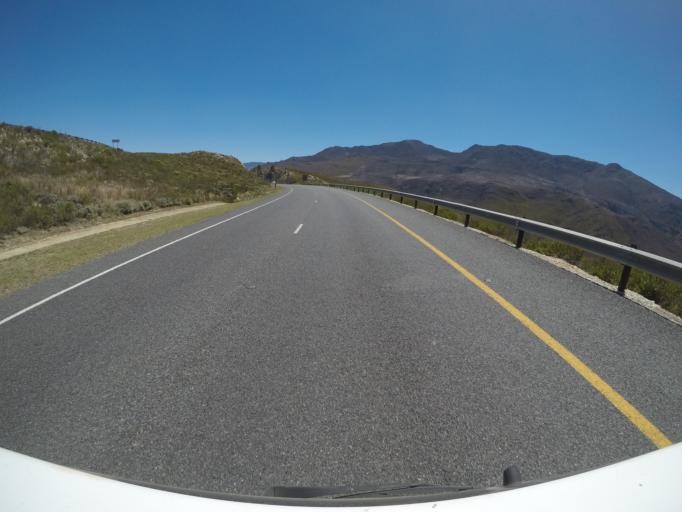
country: ZA
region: Western Cape
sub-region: Overberg District Municipality
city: Grabouw
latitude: -34.2177
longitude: 19.1738
